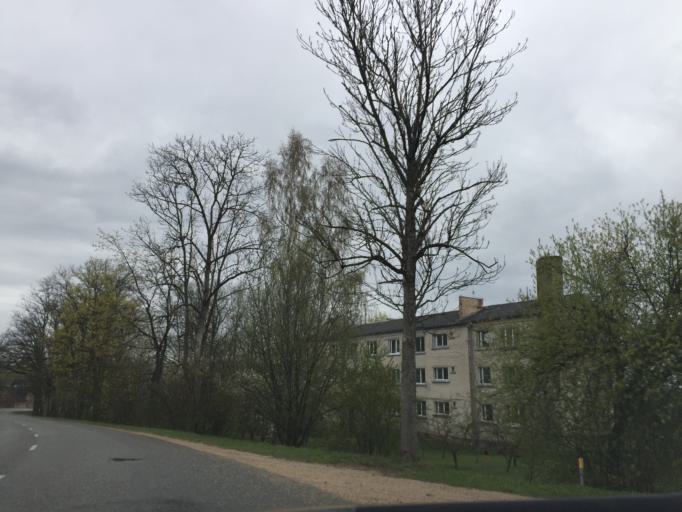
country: LV
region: Sigulda
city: Sigulda
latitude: 57.0271
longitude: 24.8172
